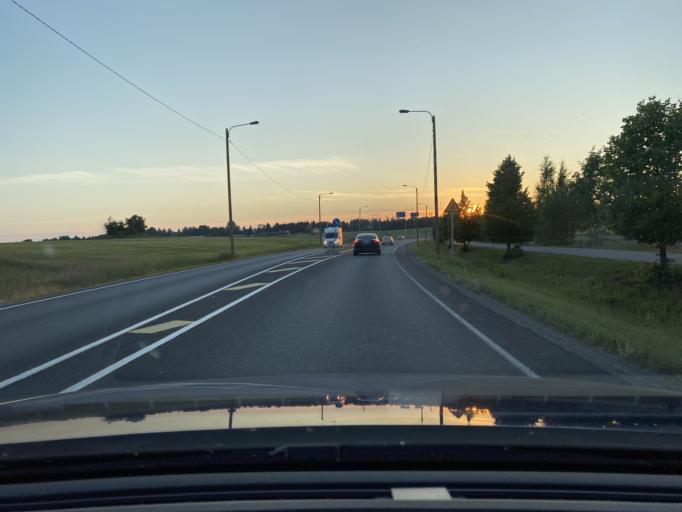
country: FI
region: Pirkanmaa
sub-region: Luoteis-Pirkanmaa
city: Ikaalinen
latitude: 61.7580
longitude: 23.0312
